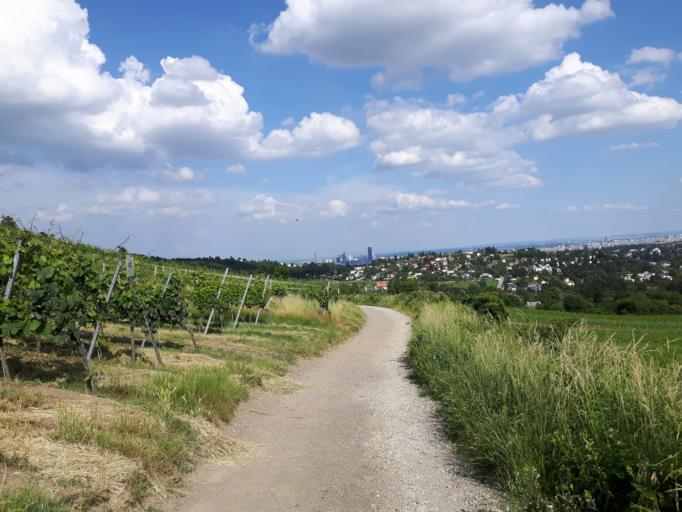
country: AT
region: Lower Austria
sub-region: Politischer Bezirk Wien-Umgebung
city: Klosterneuburg
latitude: 48.2554
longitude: 16.3005
